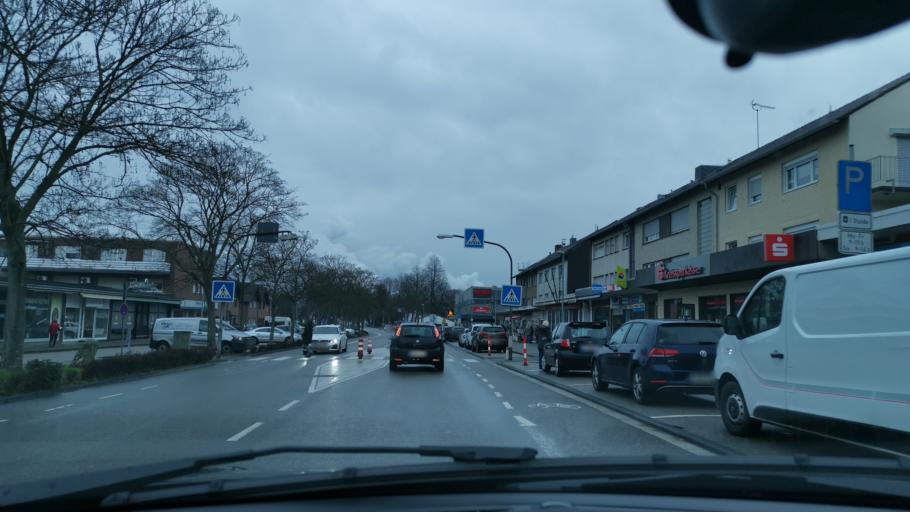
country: DE
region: North Rhine-Westphalia
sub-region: Regierungsbezirk Koln
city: Bedburg
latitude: 51.0062
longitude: 6.5518
